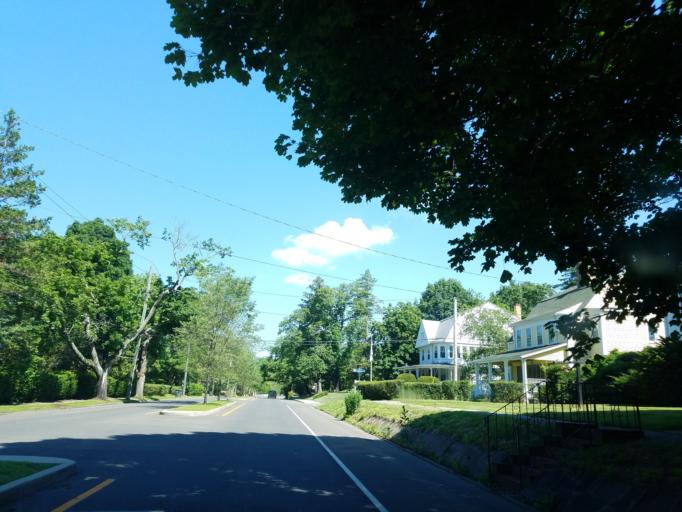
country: US
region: Connecticut
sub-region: Fairfield County
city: Bridgeport
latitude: 41.1804
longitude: -73.2157
